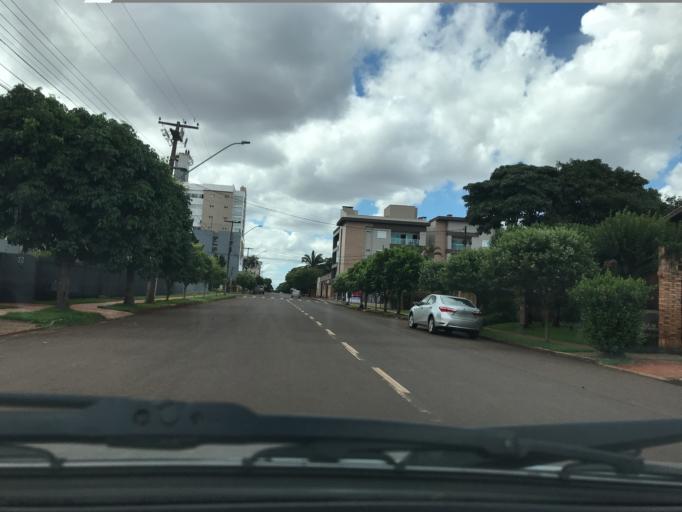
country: BR
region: Parana
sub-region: Palotina
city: Palotina
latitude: -24.2879
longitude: -53.8372
